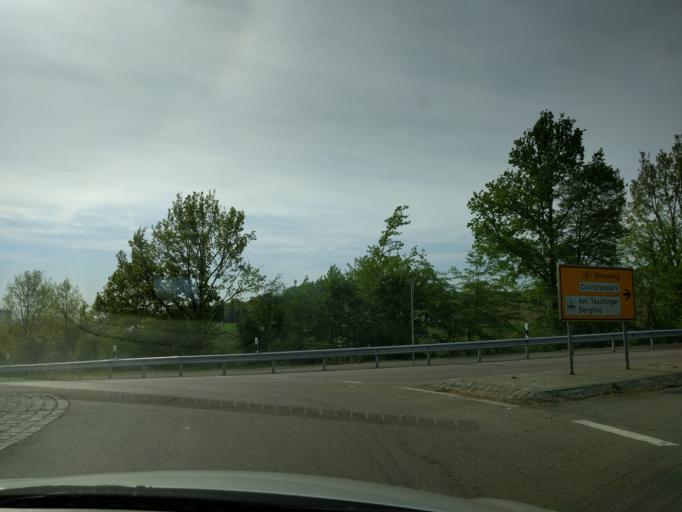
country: DE
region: Bavaria
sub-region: Upper Palatinate
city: Cham
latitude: 49.1997
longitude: 12.6590
